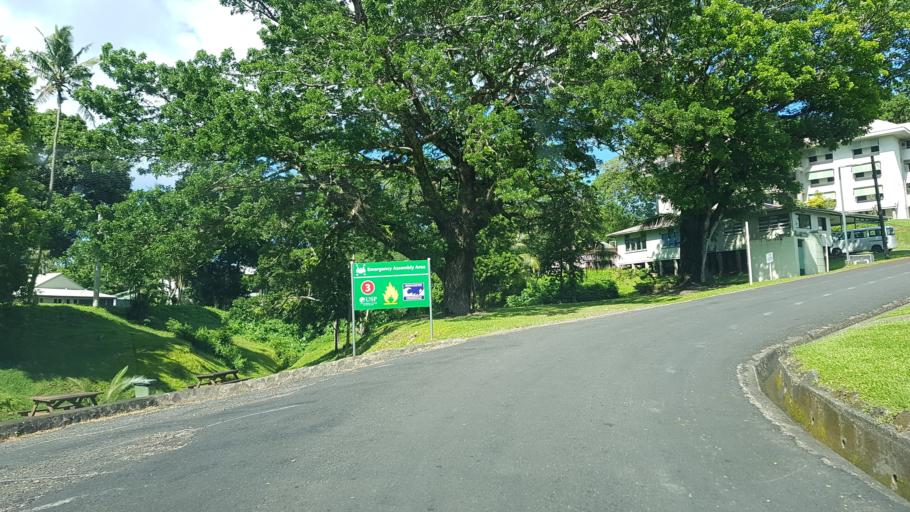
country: FJ
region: Central
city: Suva
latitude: -18.1506
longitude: 178.4437
